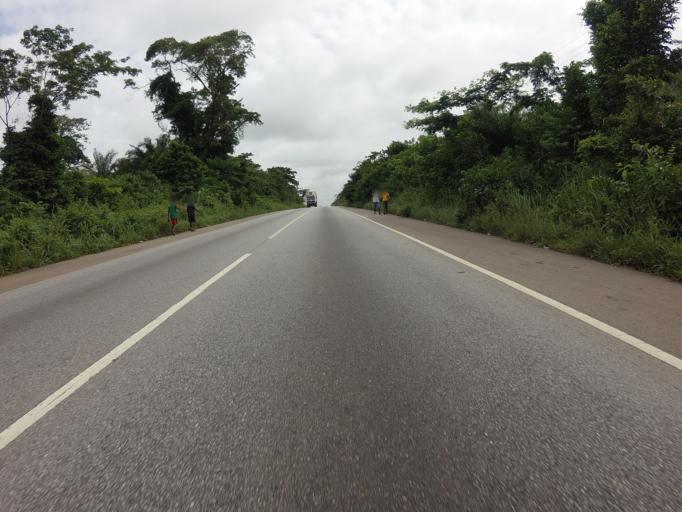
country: GH
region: Ashanti
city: Mampong
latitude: 7.0596
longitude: -1.7120
